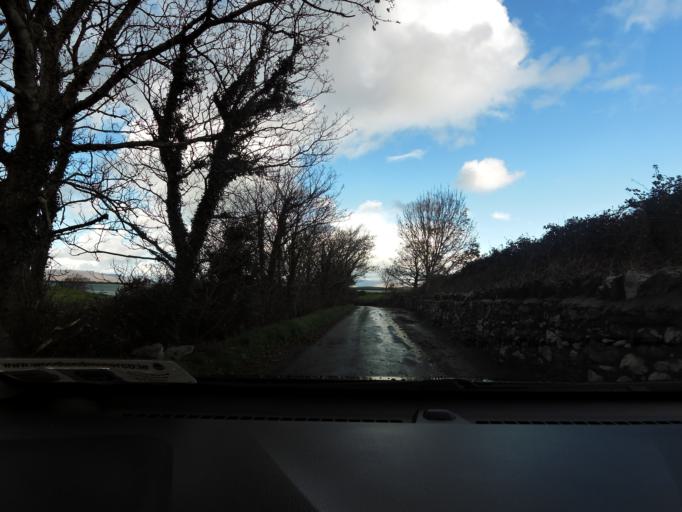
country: IE
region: Connaught
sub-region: Maigh Eo
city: Westport
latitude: 53.7808
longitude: -9.6391
